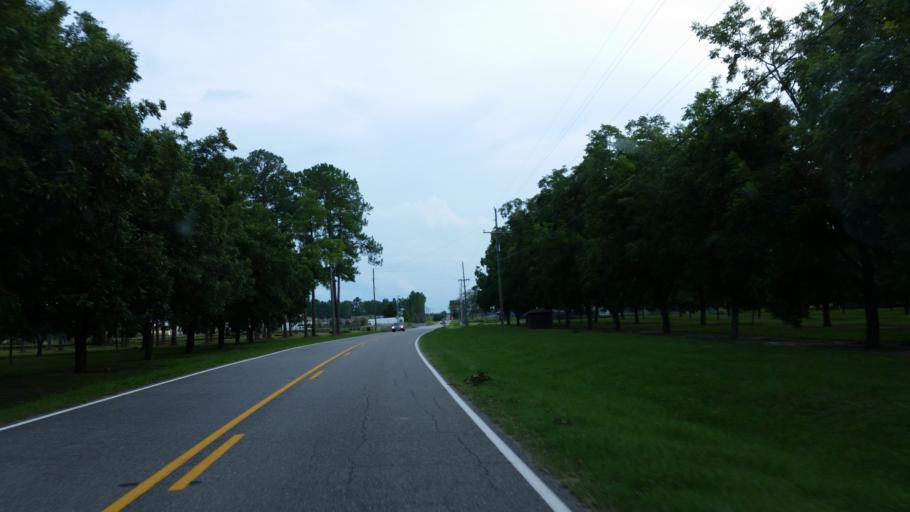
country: US
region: Georgia
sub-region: Lowndes County
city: Hahira
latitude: 31.0008
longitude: -83.3871
